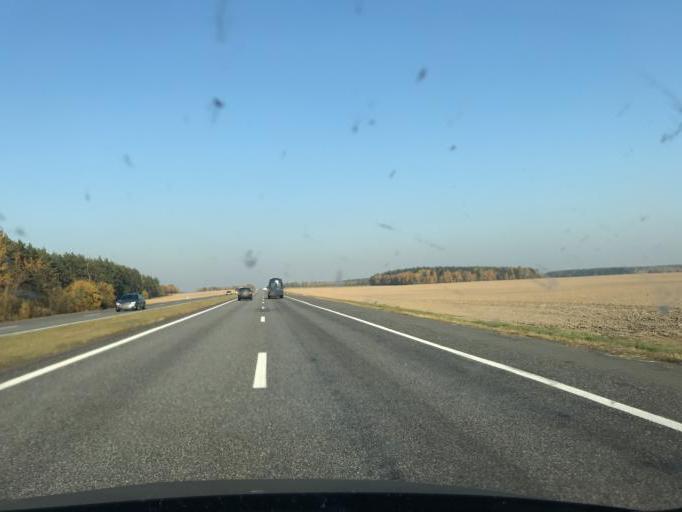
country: BY
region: Minsk
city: Haradzyeya
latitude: 53.3650
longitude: 26.4832
